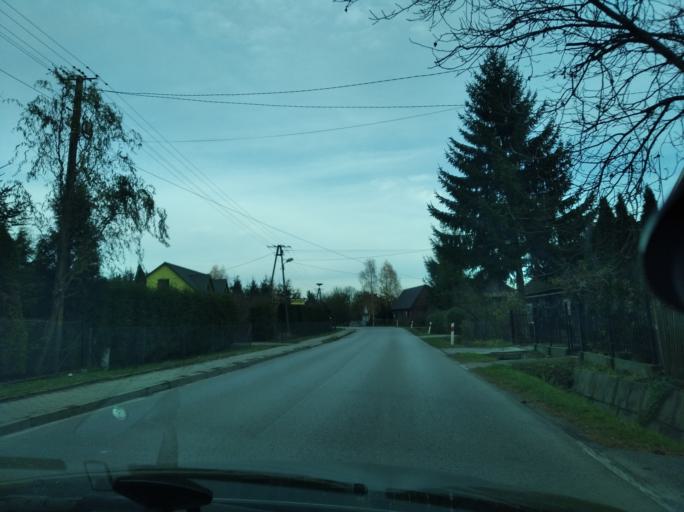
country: PL
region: Subcarpathian Voivodeship
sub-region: Powiat przeworski
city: Przeworsk
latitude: 50.0514
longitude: 22.4708
